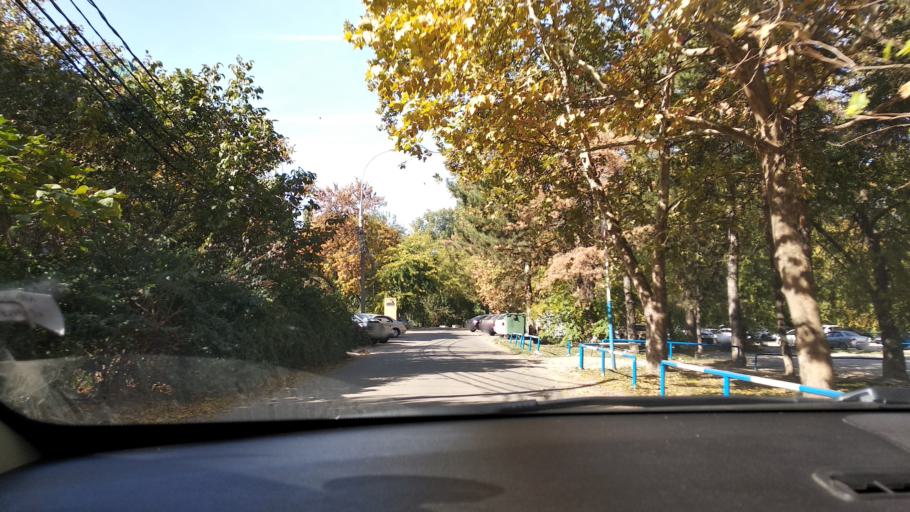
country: RU
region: Adygeya
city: Yablonovskiy
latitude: 45.0166
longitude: 38.9544
